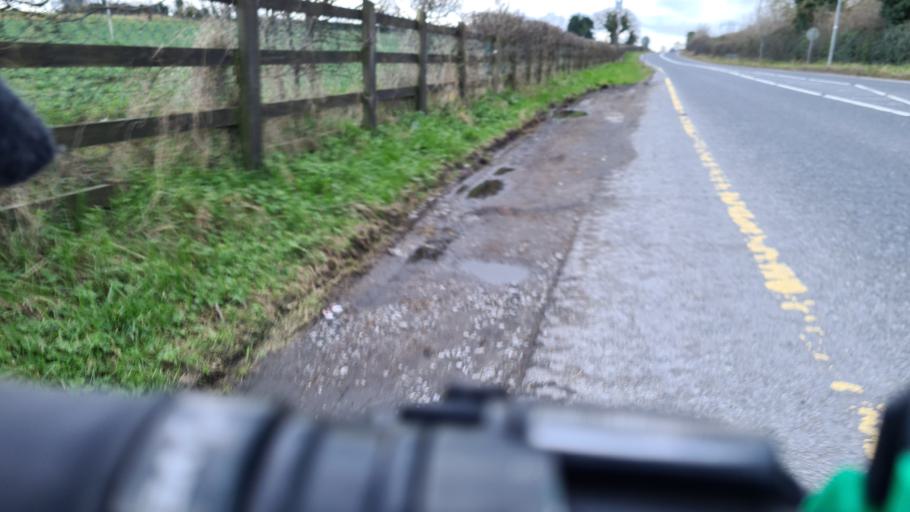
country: IE
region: Leinster
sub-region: Kildare
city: Maynooth
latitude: 53.3493
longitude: -6.5994
